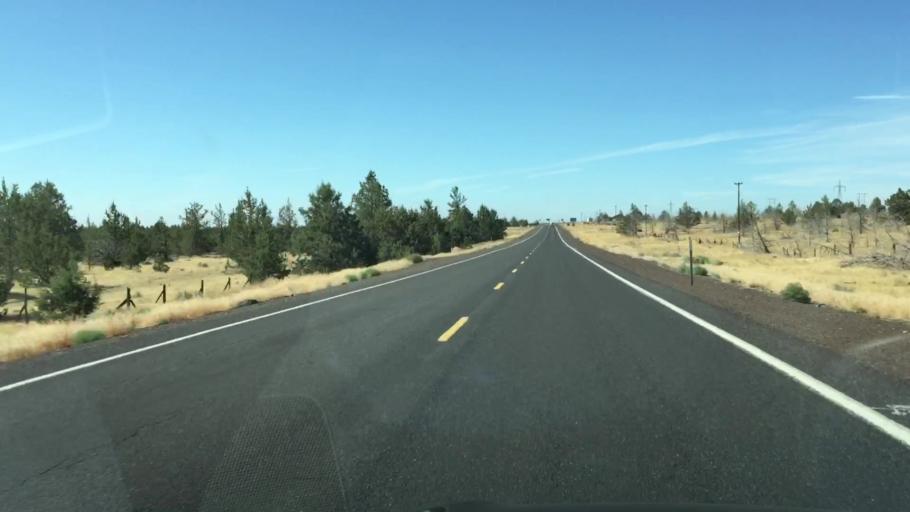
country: US
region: Oregon
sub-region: Jefferson County
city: Madras
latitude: 44.9289
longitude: -120.9381
